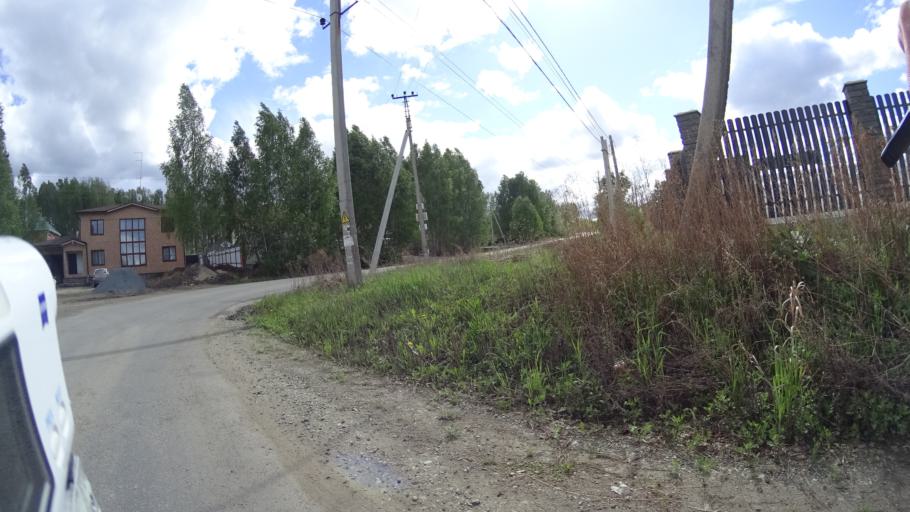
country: RU
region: Chelyabinsk
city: Sargazy
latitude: 55.1521
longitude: 61.2399
